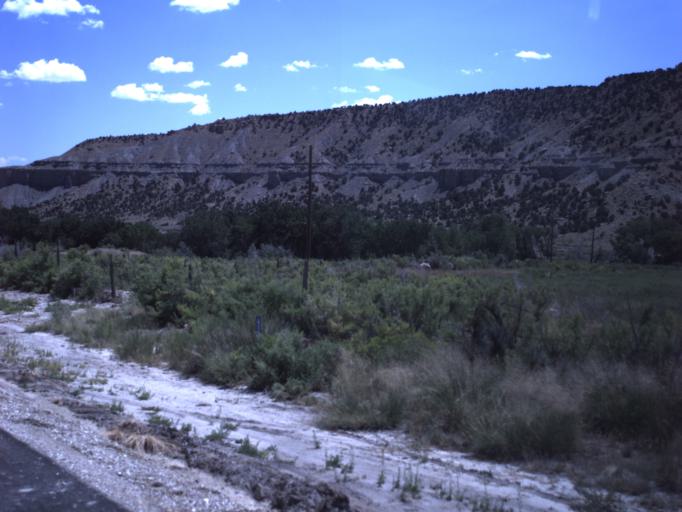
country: US
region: Utah
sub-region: Emery County
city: Orangeville
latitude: 39.2642
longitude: -111.1243
